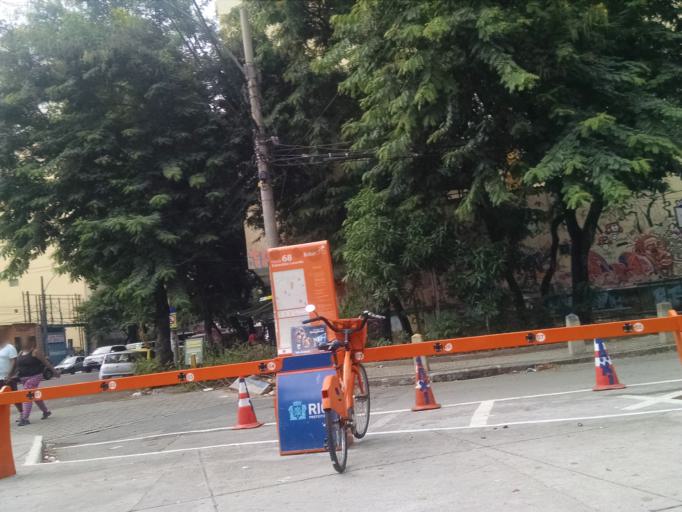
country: BR
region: Rio de Janeiro
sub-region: Rio De Janeiro
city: Rio de Janeiro
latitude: -22.9375
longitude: -43.1903
